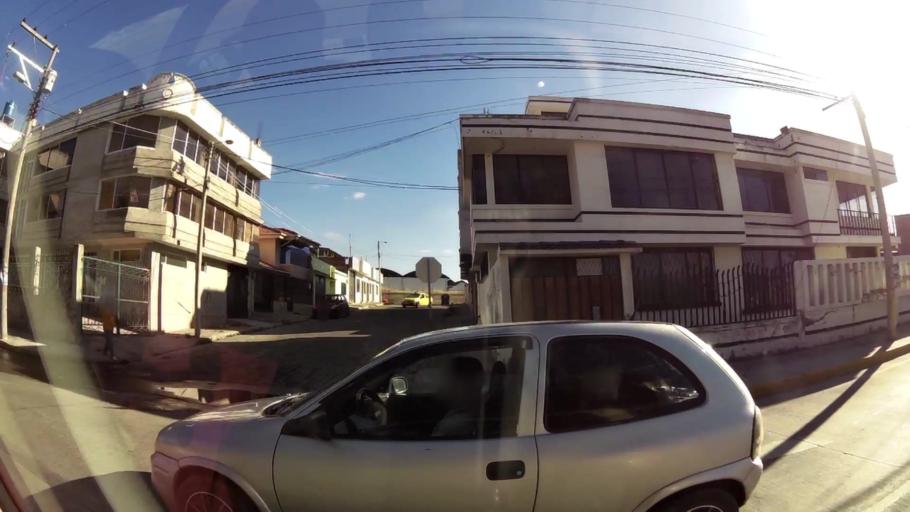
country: EC
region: Chimborazo
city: Riobamba
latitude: -1.6686
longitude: -78.6667
